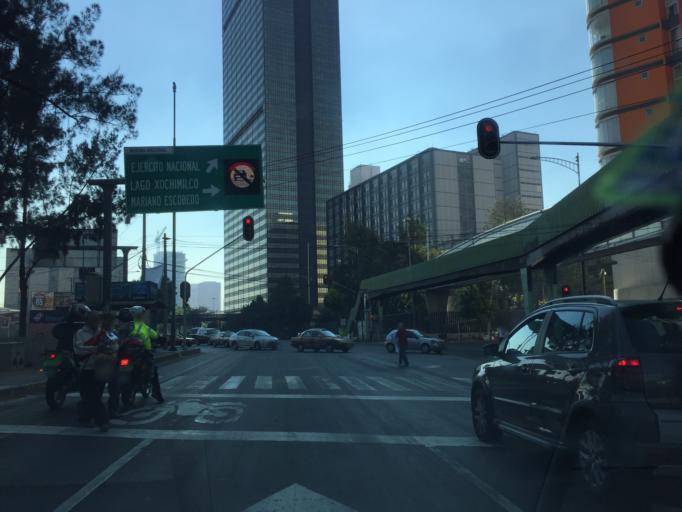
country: MX
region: Mexico City
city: Miguel Hidalgo
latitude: 19.4410
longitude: -99.1765
